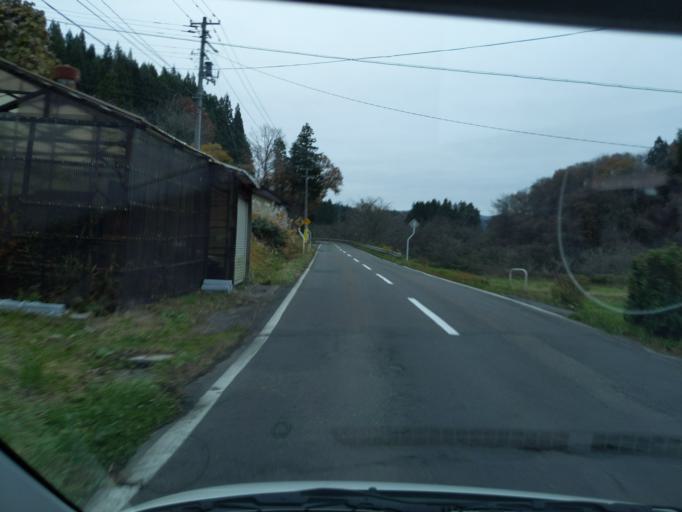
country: JP
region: Iwate
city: Kitakami
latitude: 39.2319
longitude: 141.2955
